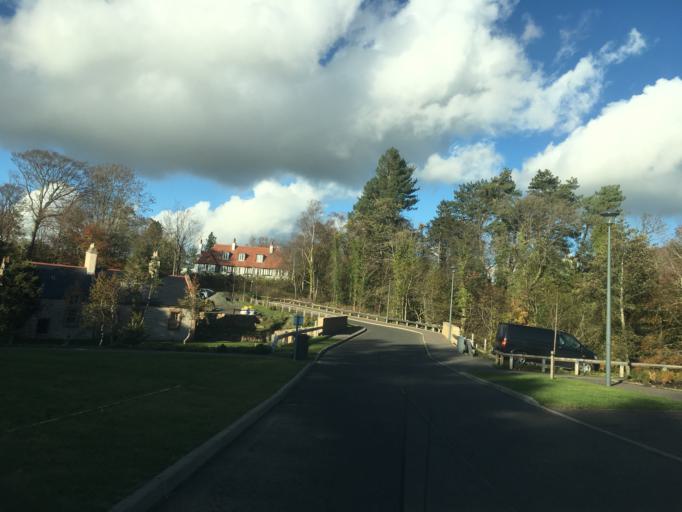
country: GB
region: Scotland
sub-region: Edinburgh
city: Colinton
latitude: 55.9019
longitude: -3.2496
